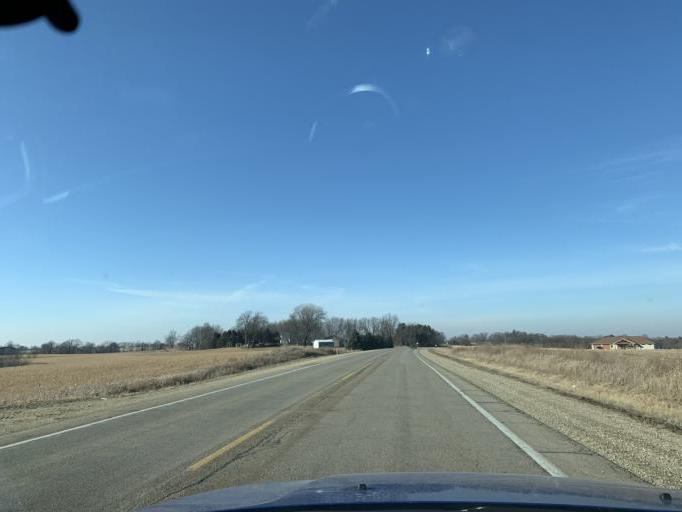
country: US
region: Wisconsin
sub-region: Green County
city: Monroe
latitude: 42.6228
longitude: -89.6641
